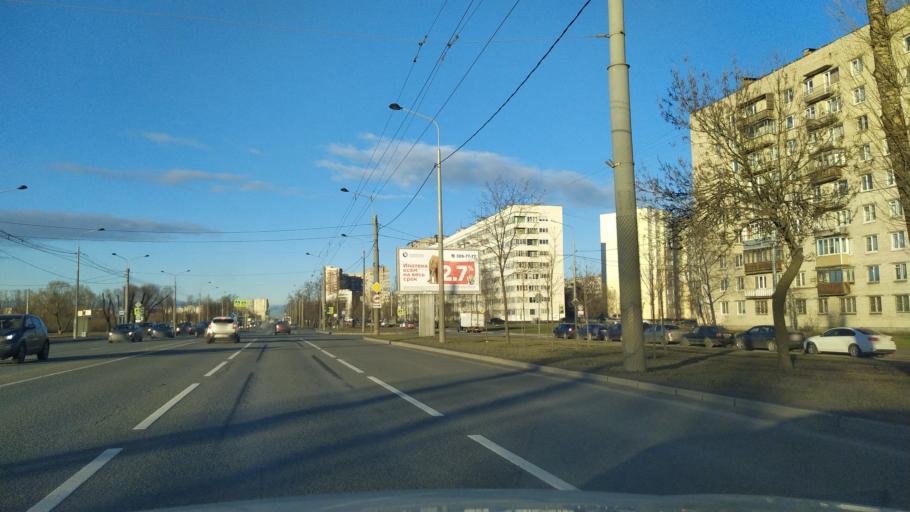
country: RU
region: St.-Petersburg
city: Uritsk
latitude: 59.8357
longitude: 30.1982
